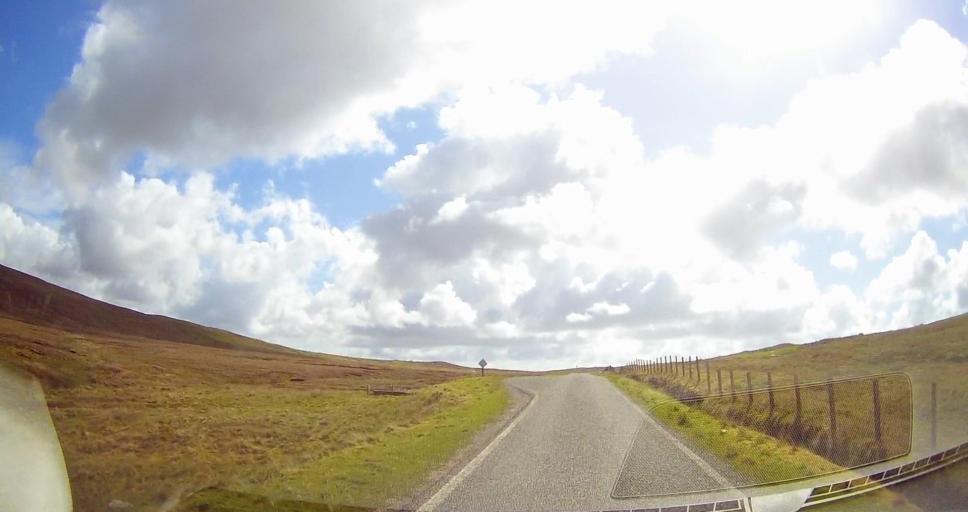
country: GB
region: Scotland
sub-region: Shetland Islands
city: Lerwick
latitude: 60.5062
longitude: -1.3893
